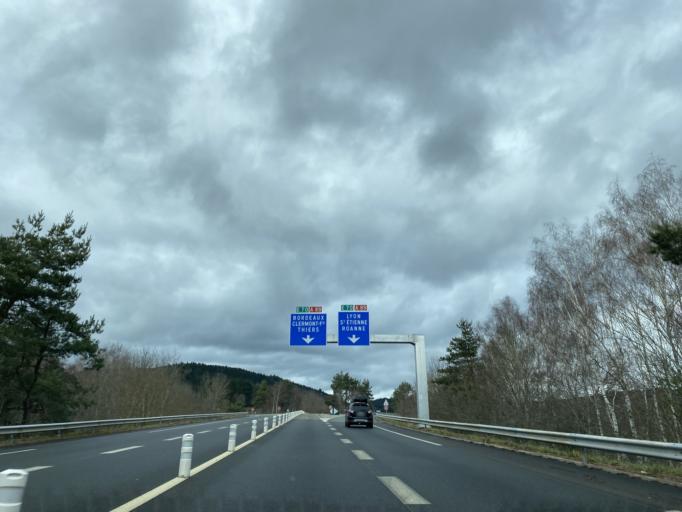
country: FR
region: Rhone-Alpes
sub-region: Departement de la Loire
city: Noiretable
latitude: 45.8515
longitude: 3.7924
